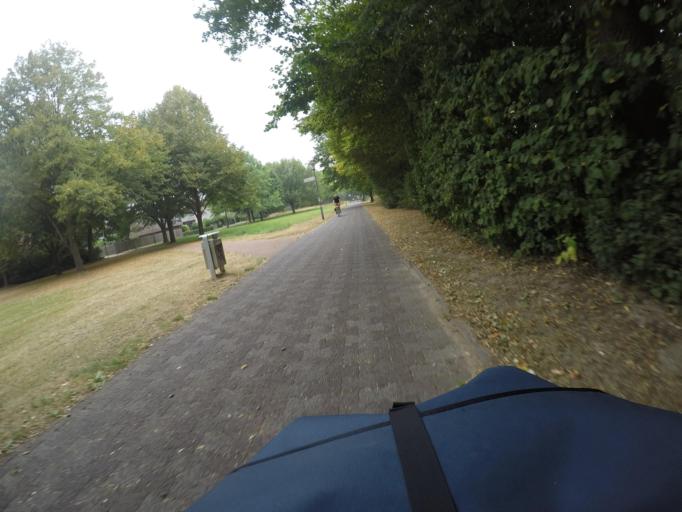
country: DE
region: North Rhine-Westphalia
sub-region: Regierungsbezirk Dusseldorf
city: Krefeld
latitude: 51.3074
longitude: 6.5957
